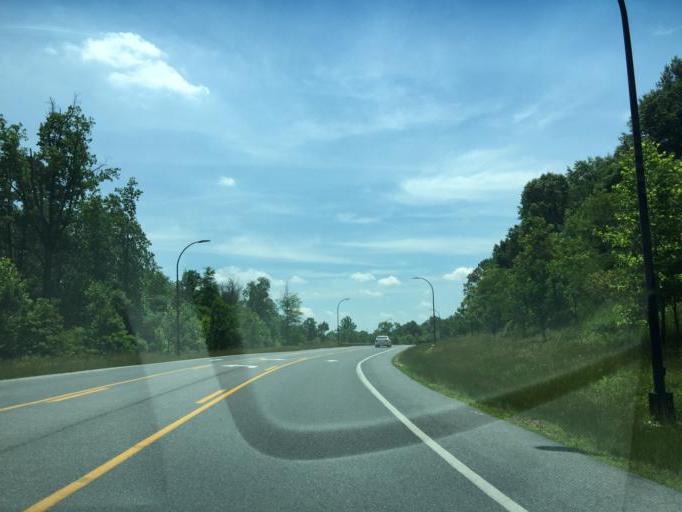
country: US
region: Maryland
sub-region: Howard County
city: Hanover
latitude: 39.1866
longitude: -76.6971
